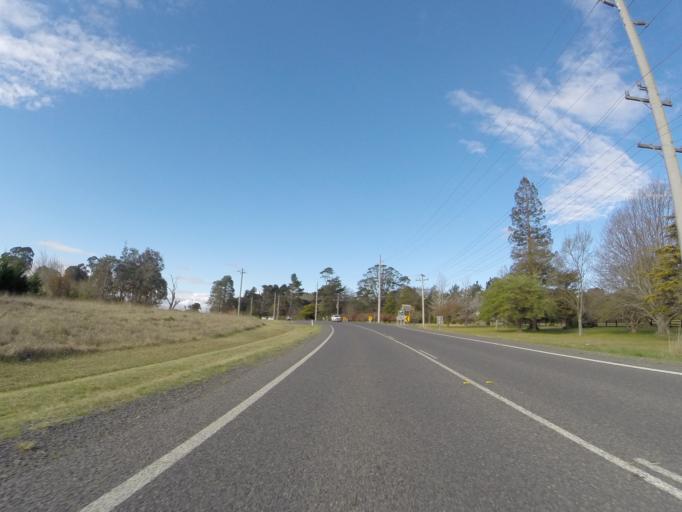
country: AU
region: New South Wales
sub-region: Wingecarribee
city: Moss Vale
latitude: -34.5616
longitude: 150.3422
